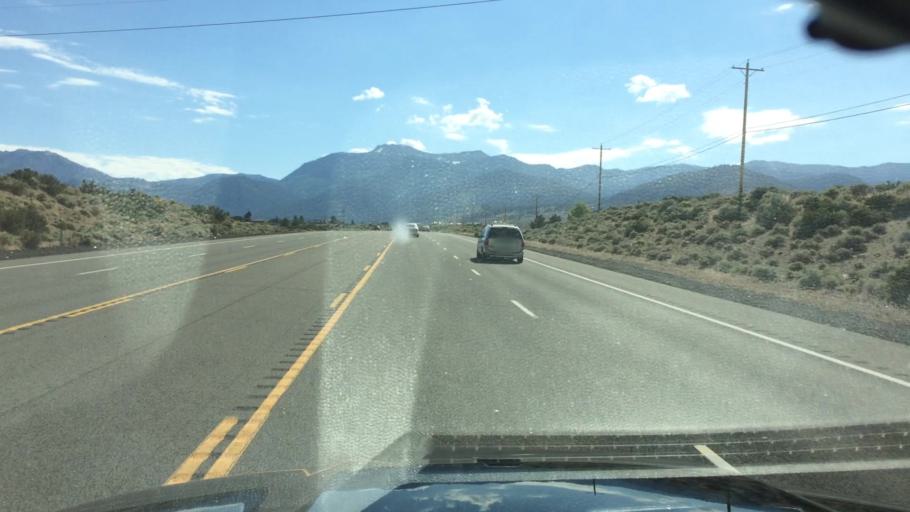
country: US
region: Nevada
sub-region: Washoe County
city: Reno
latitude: 39.3909
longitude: -119.8006
